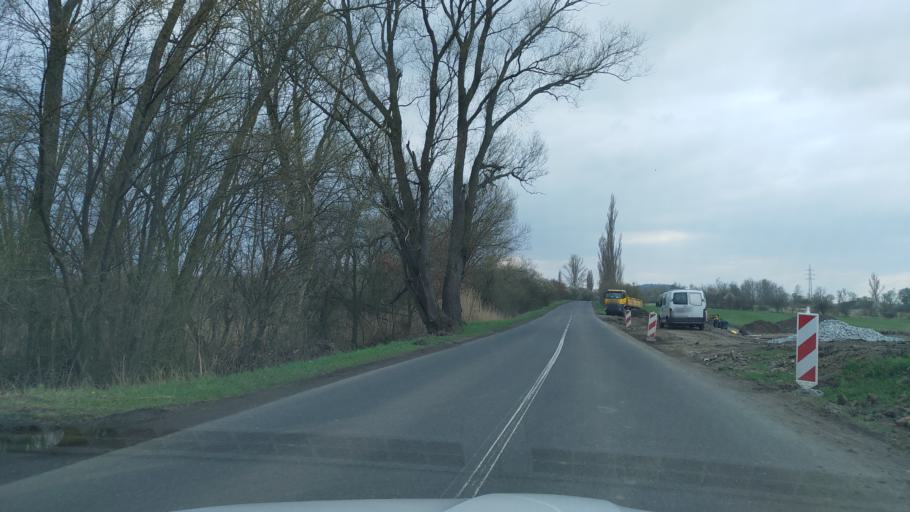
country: CZ
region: Ustecky
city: Chabarovice
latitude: 50.6711
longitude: 13.9322
